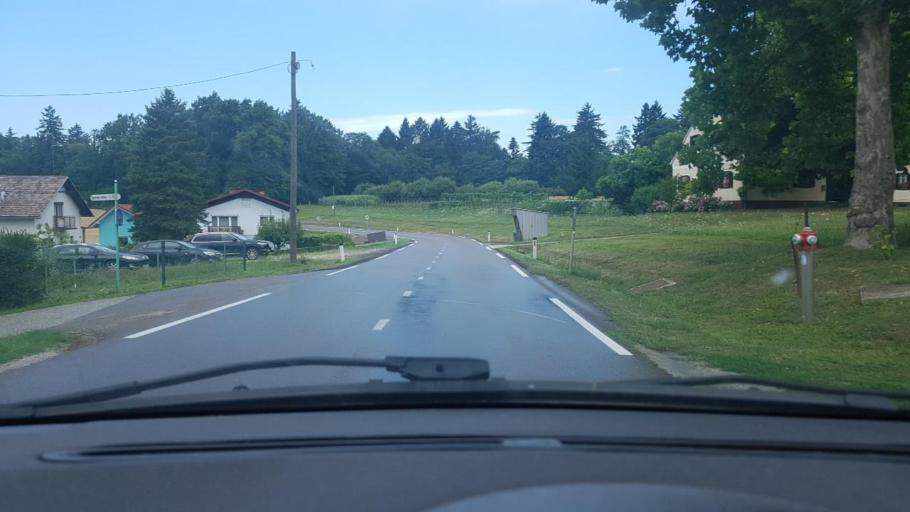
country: AT
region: Styria
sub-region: Politischer Bezirk Suedoststeiermark
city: Mureck
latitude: 46.6951
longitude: 15.7800
